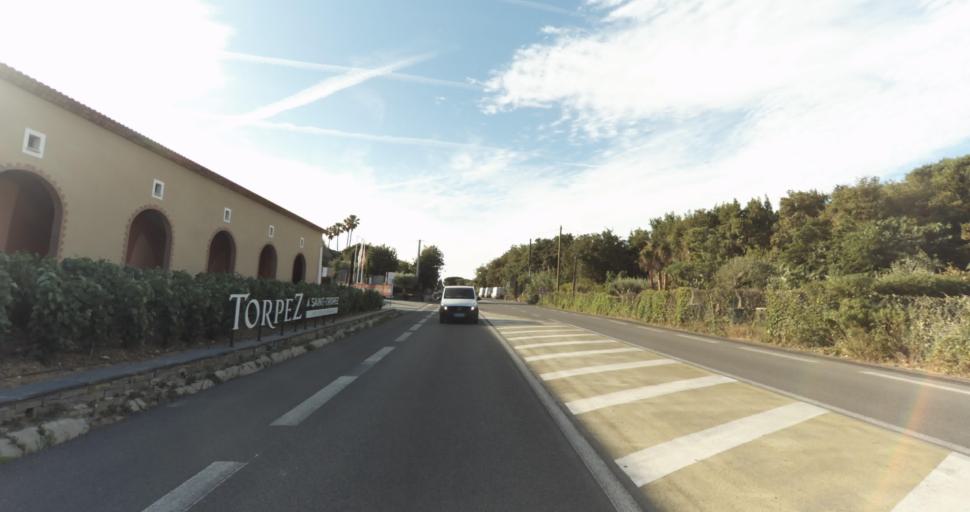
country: FR
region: Provence-Alpes-Cote d'Azur
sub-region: Departement du Var
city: Saint-Tropez
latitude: 43.2565
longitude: 6.6352
